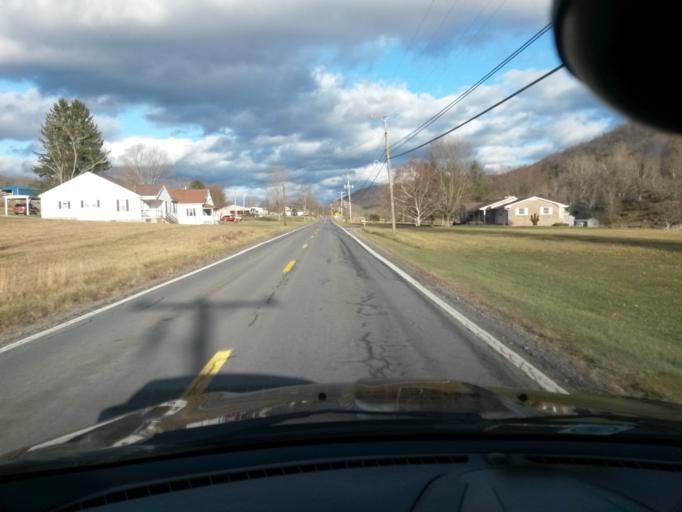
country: US
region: Virginia
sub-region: Giles County
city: Pearisburg
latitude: 37.4447
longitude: -80.6837
